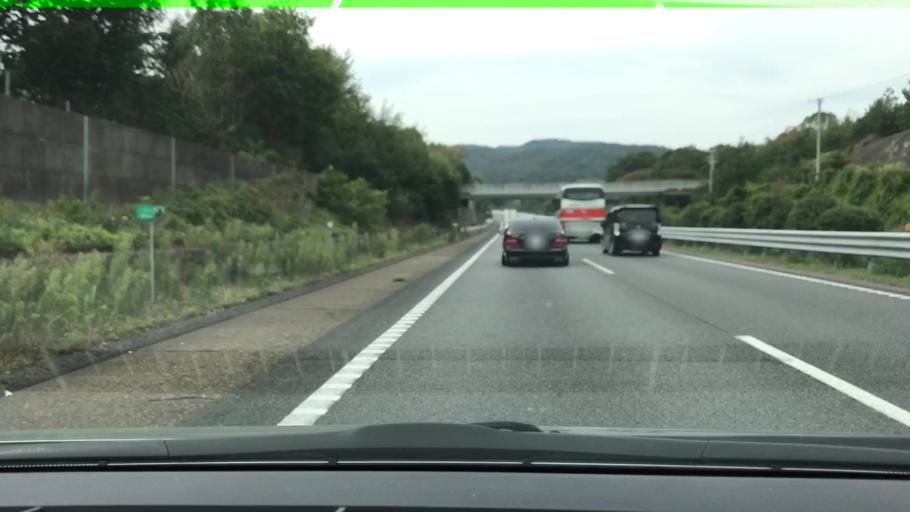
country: JP
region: Hyogo
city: Aioi
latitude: 34.8247
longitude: 134.4682
